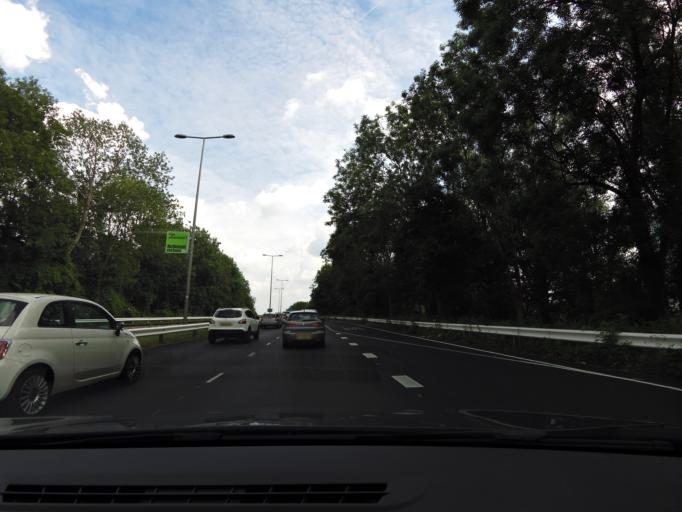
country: NL
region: South Holland
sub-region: Gemeente Barendrecht
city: Barendrecht
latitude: 51.8786
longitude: 4.5039
